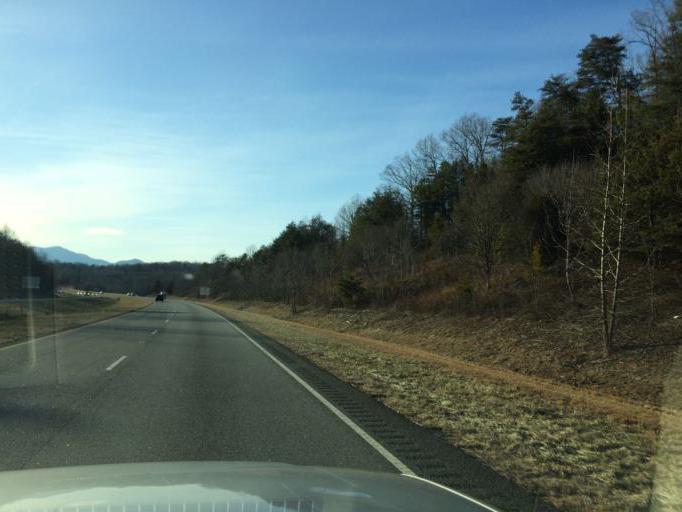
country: US
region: North Carolina
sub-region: Polk County
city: Columbus
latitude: 35.2909
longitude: -82.0873
